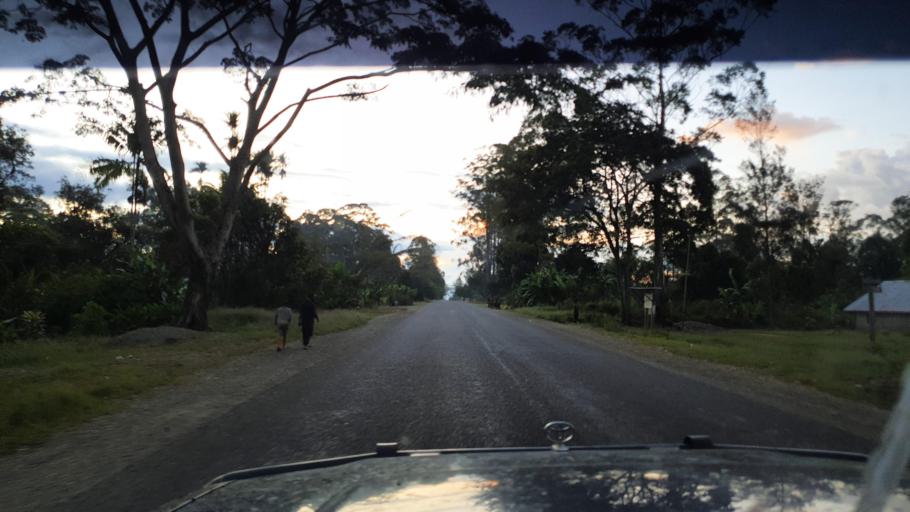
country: PG
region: Jiwaka
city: Minj
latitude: -5.8305
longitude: 144.5061
